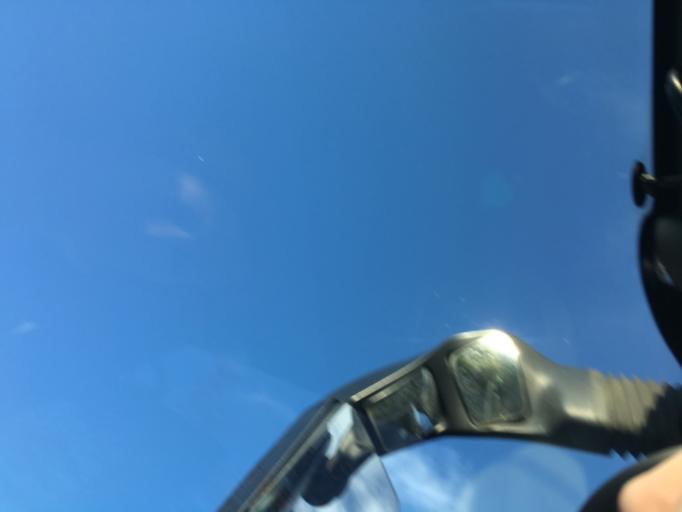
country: SI
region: Ruse
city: Ruse
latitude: 46.5450
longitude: 15.5091
